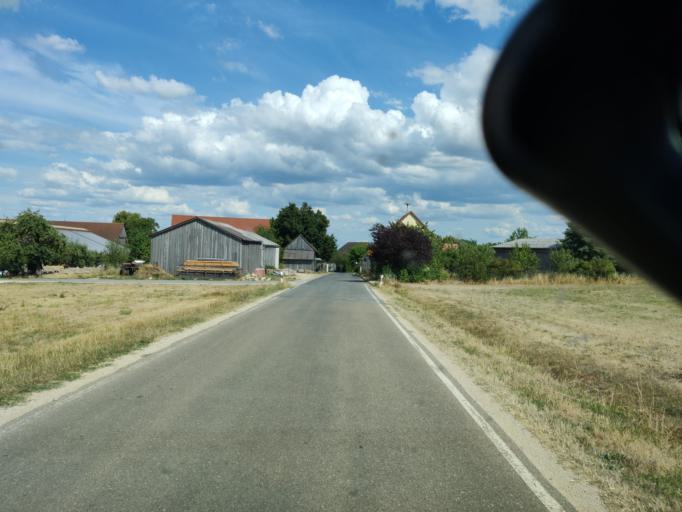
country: DE
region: Bavaria
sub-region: Regierungsbezirk Mittelfranken
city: Thalmassing
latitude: 49.0651
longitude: 11.2437
